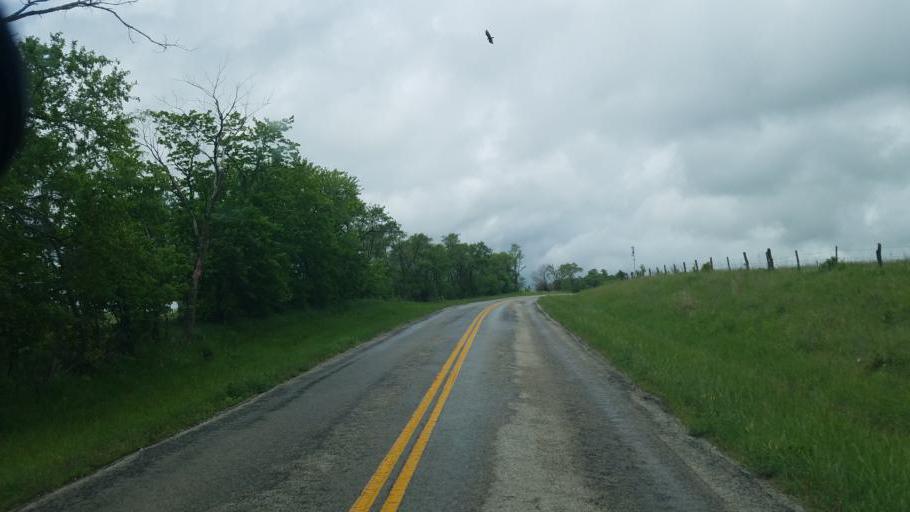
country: US
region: Missouri
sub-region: Mercer County
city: Princeton
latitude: 40.5150
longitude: -93.7167
